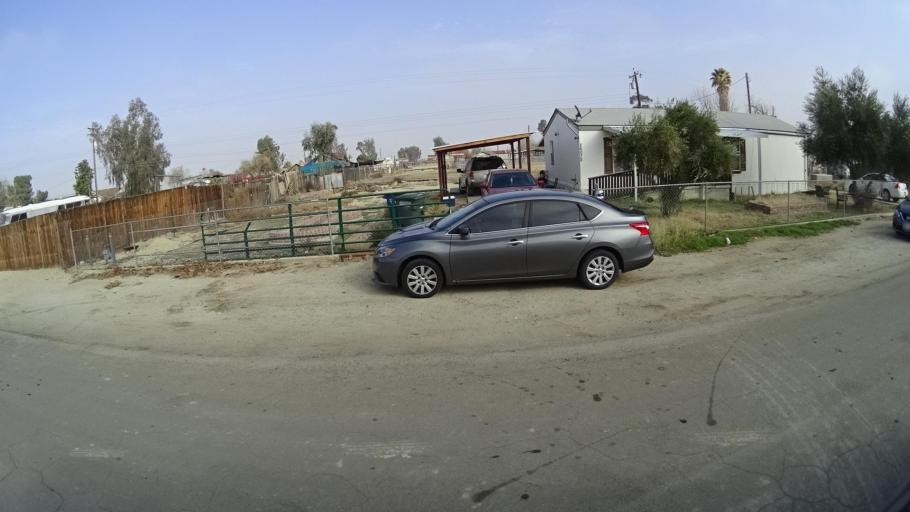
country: US
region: California
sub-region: Kern County
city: Ford City
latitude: 35.2054
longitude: -119.4063
